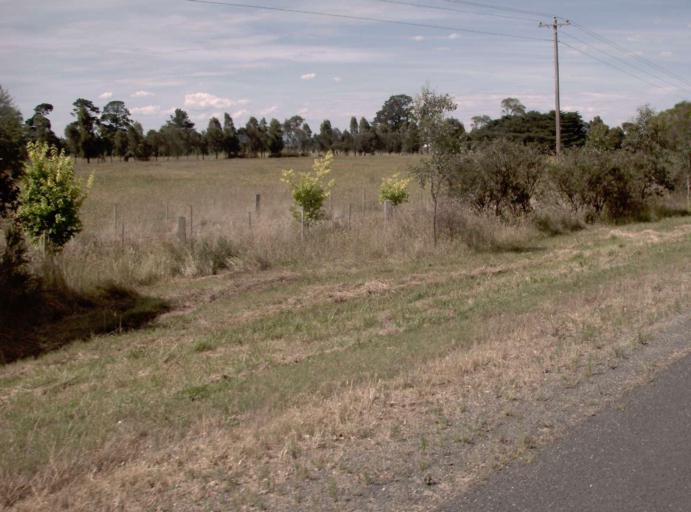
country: AU
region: Victoria
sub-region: East Gippsland
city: Bairnsdale
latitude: -37.8457
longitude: 147.5728
